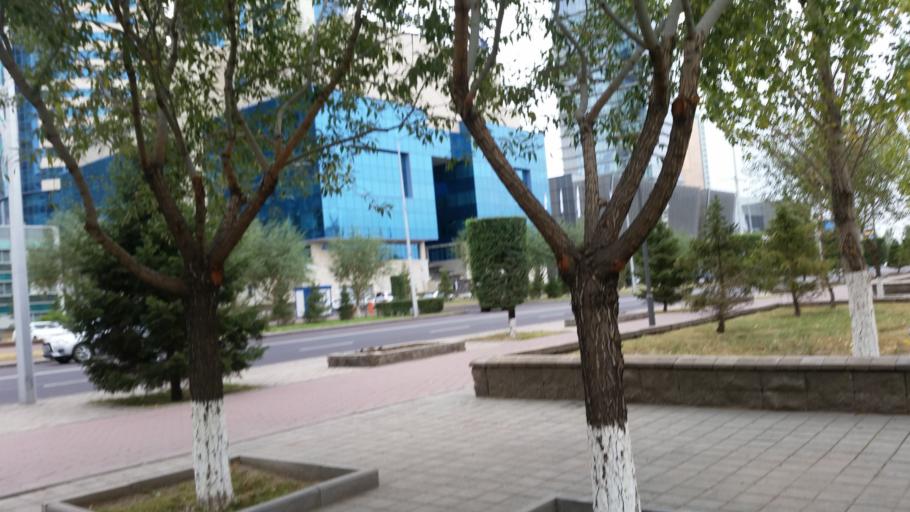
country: KZ
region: Astana Qalasy
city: Astana
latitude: 51.1320
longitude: 71.4231
